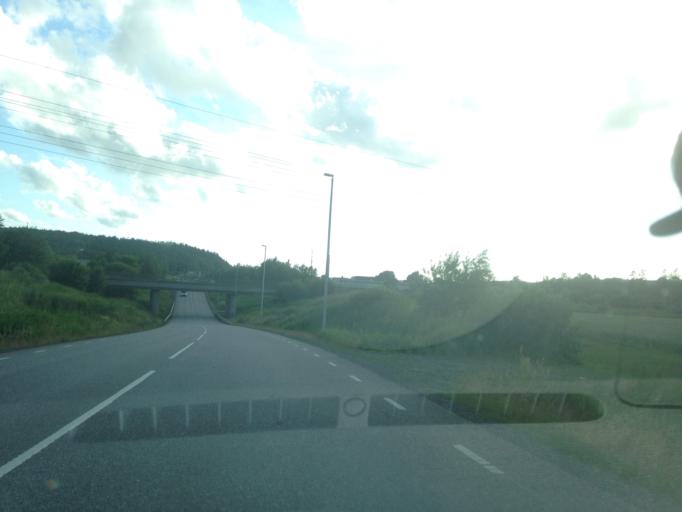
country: SE
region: Halland
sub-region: Kungsbacka Kommun
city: Fjaeras kyrkby
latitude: 57.4370
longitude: 12.1614
